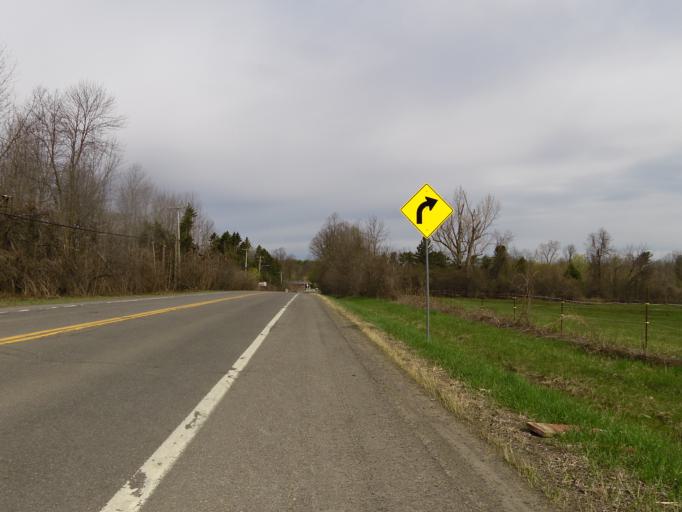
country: CA
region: Quebec
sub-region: Laurentides
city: Oka
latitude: 45.4713
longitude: -74.1218
